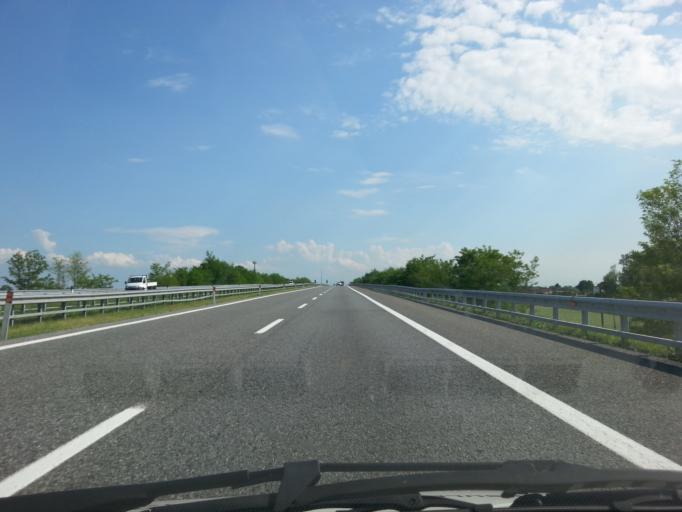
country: IT
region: Piedmont
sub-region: Provincia di Cuneo
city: Caramagna Piemonte
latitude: 44.8119
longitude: 7.7514
